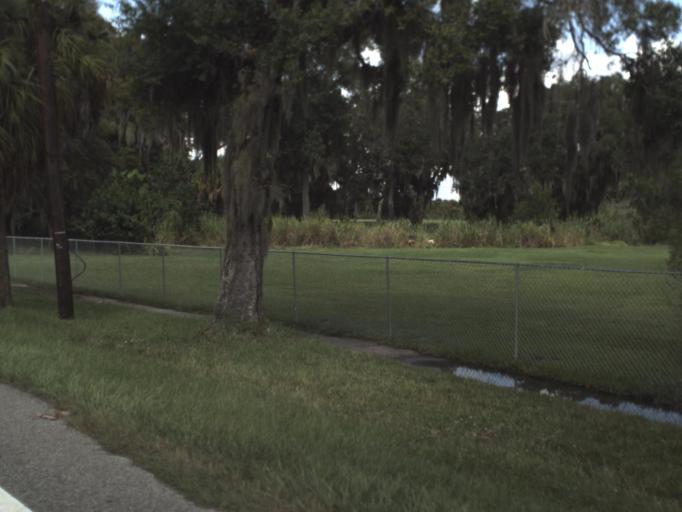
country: US
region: Florida
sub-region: Manatee County
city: Samoset
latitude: 27.4810
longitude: -82.5466
